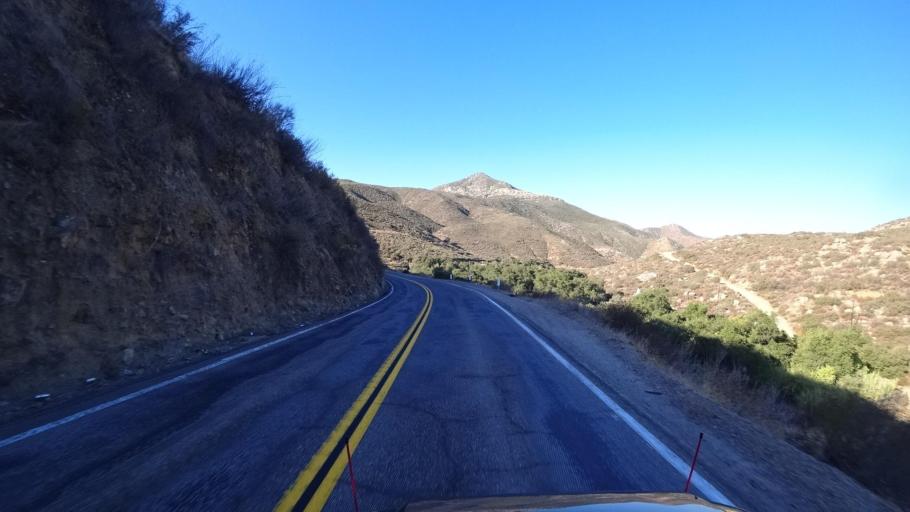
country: MX
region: Baja California
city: Tecate
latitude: 32.5958
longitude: -116.6610
